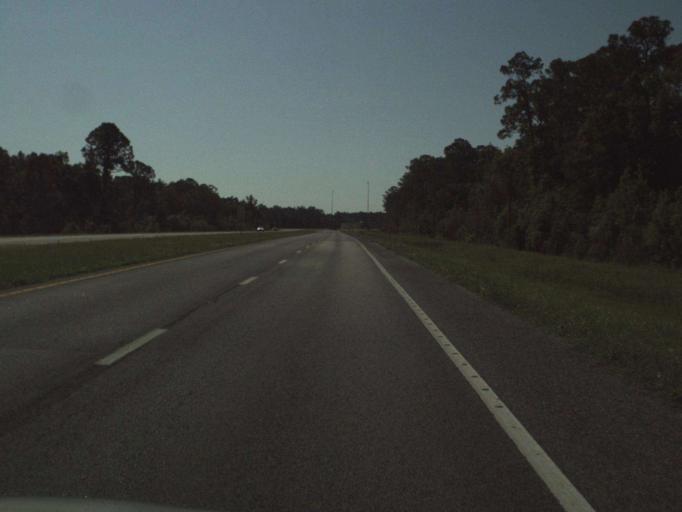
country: US
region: Florida
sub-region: Orange County
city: Christmas
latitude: 28.4589
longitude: -80.9875
